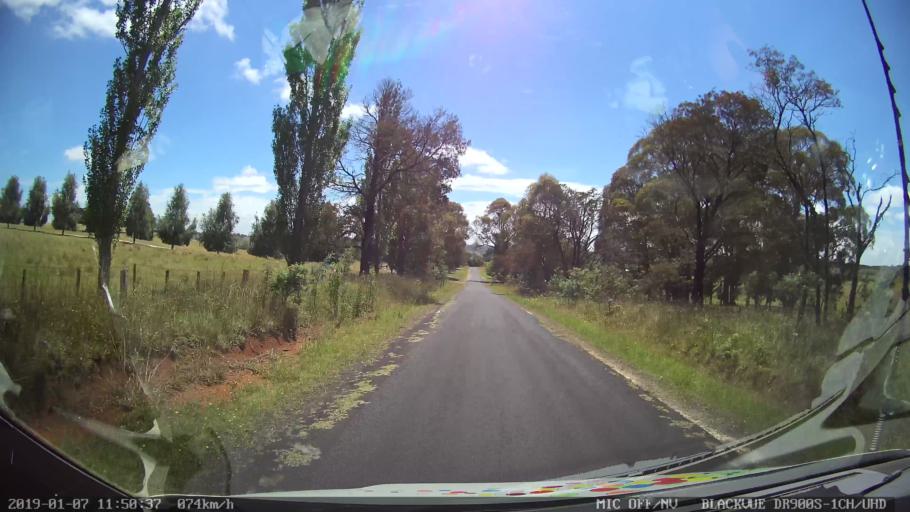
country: AU
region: New South Wales
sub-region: Guyra
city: Guyra
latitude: -30.3120
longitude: 151.6380
